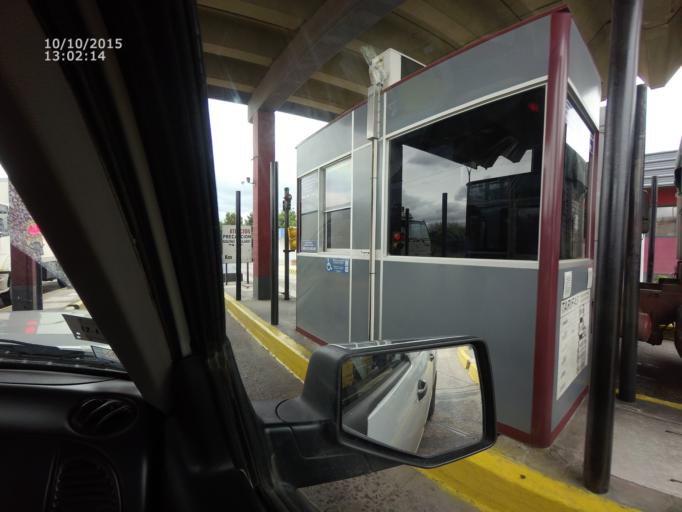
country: AR
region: Salta
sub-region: Departamento de General Guemes
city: General Martin Miguel de Guemes
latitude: -24.8143
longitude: -65.0159
